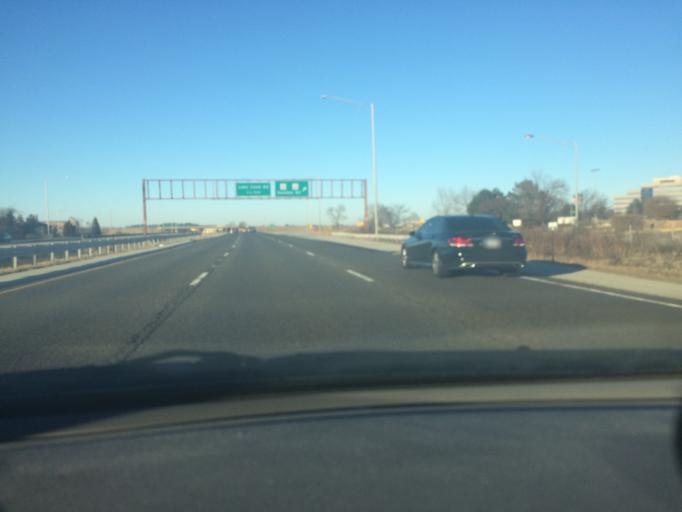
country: US
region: Illinois
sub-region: Cook County
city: Palatine
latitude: 42.1339
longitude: -88.0047
